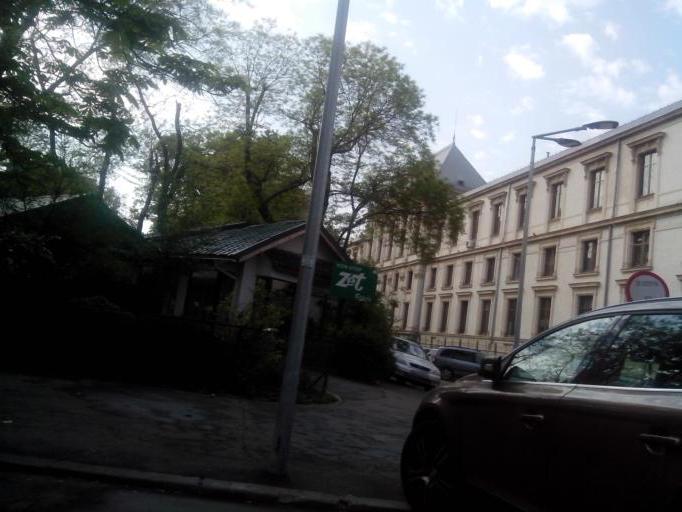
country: RO
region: Bucuresti
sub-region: Municipiul Bucuresti
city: Bucuresti
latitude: 44.4280
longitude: 26.0993
